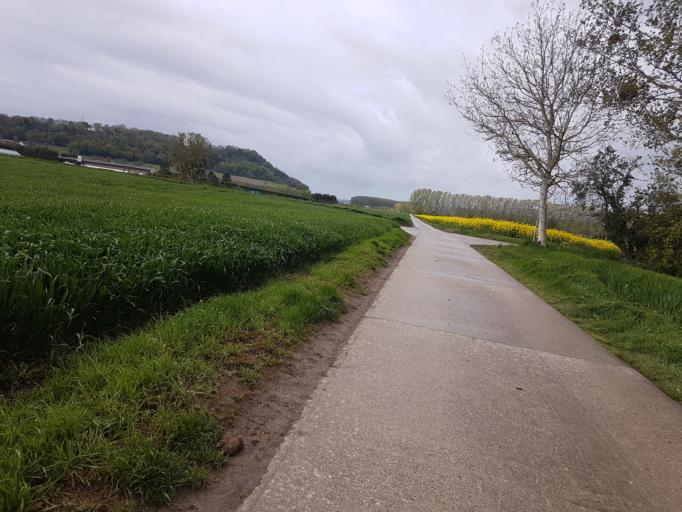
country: CH
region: Vaud
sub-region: Jura-Nord vaudois District
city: Montagny
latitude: 46.7522
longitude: 6.6064
